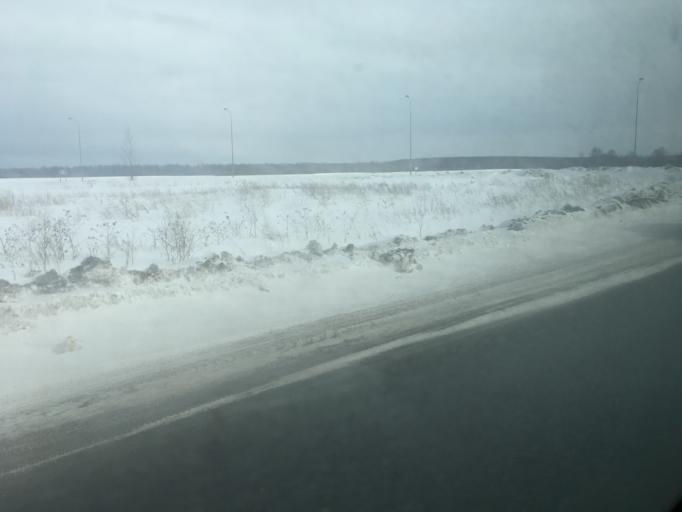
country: RU
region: Tatarstan
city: Nizhniye Vyazovyye
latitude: 55.7646
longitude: 48.5349
